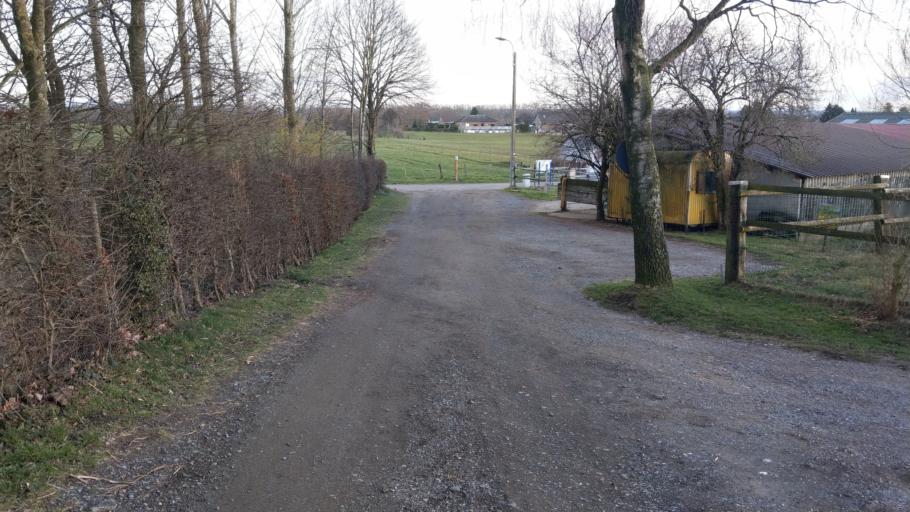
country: BE
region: Wallonia
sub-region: Province de Liege
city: Raeren
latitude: 50.7217
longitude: 6.1122
